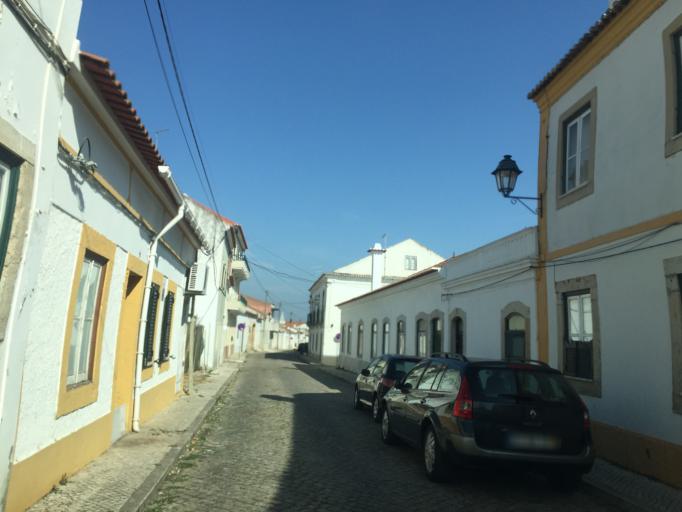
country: PT
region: Santarem
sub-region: Salvaterra de Magos
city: Salvaterra de Magos
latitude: 39.0292
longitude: -8.7915
